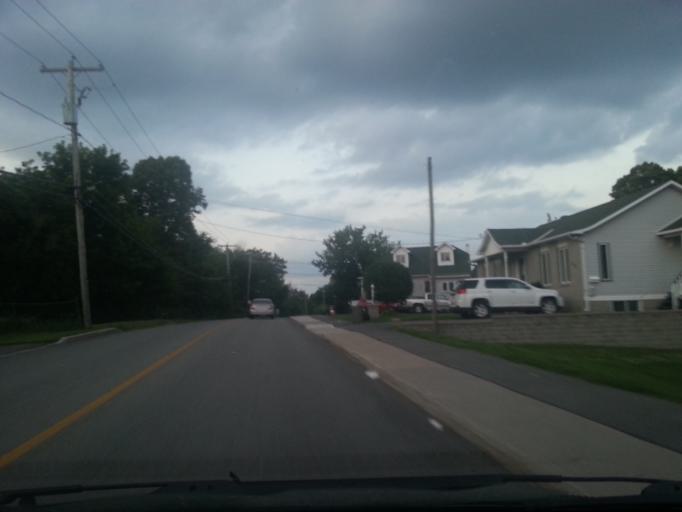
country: CA
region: Quebec
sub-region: Outaouais
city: Gatineau
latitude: 45.4993
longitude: -75.6035
